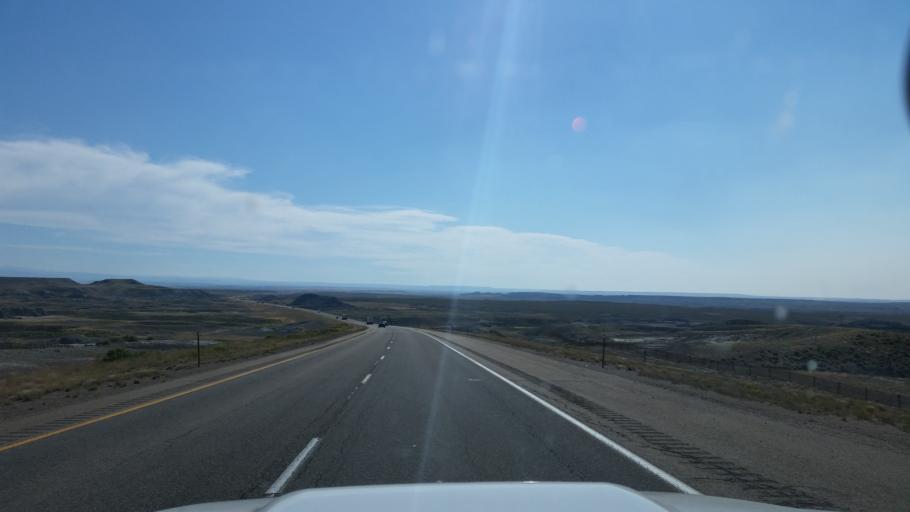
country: US
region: Wyoming
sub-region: Uinta County
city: Lyman
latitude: 41.4268
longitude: -110.1268
